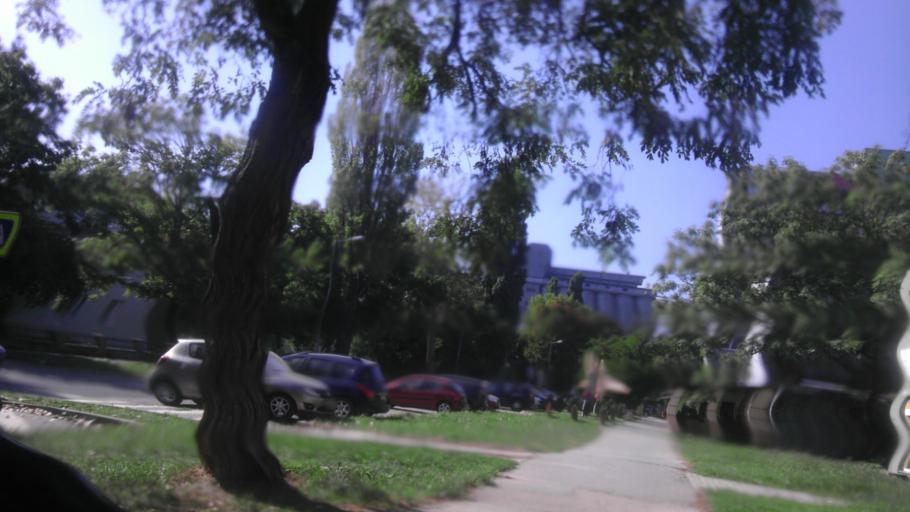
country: SK
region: Bratislavsky
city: Bratislava
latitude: 48.1809
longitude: 17.1360
